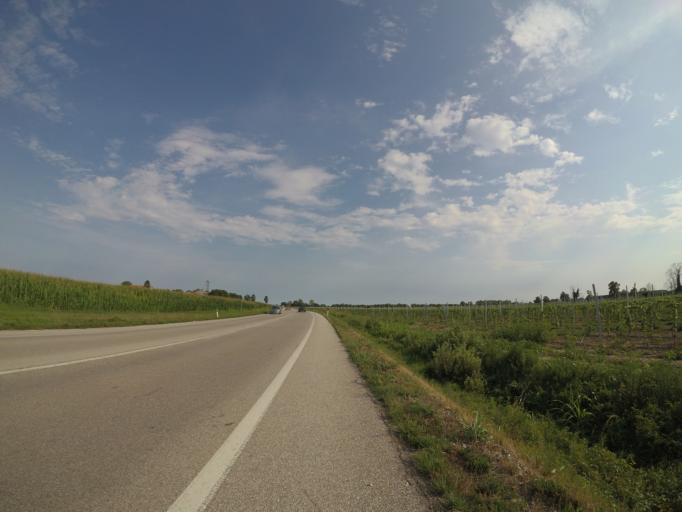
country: IT
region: Friuli Venezia Giulia
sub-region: Provincia di Udine
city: Codroipo
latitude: 45.9344
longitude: 12.9784
